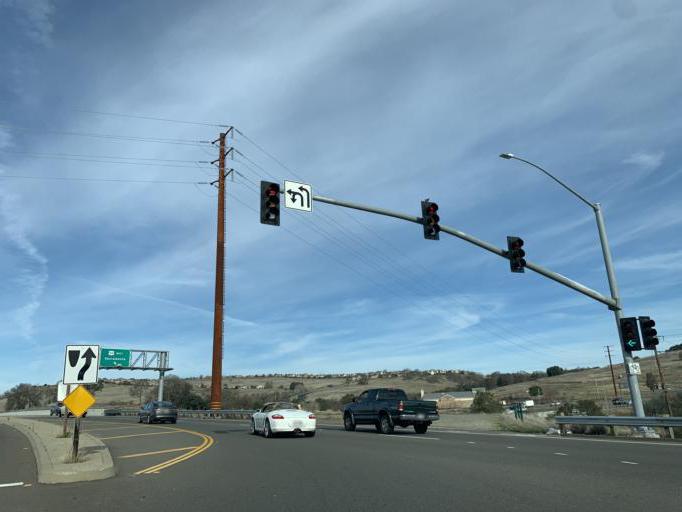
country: US
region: California
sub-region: El Dorado County
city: El Dorado Hills
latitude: 38.6569
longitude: -121.0541
